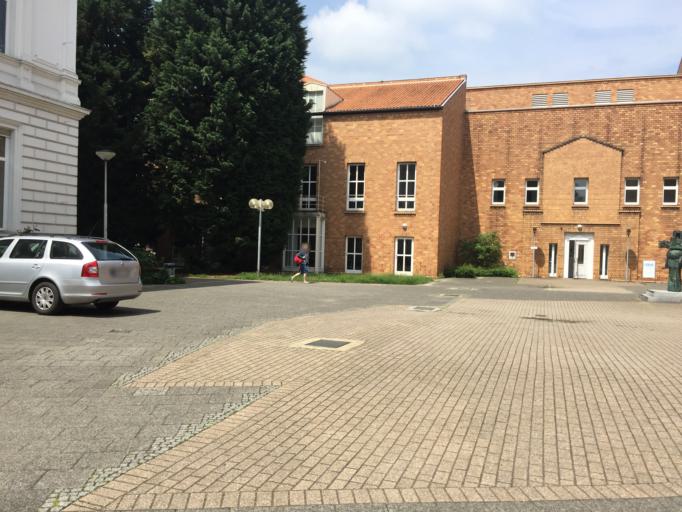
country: DE
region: North Rhine-Westphalia
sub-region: Regierungsbezirk Dusseldorf
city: Viersen
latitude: 51.2584
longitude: 6.3920
